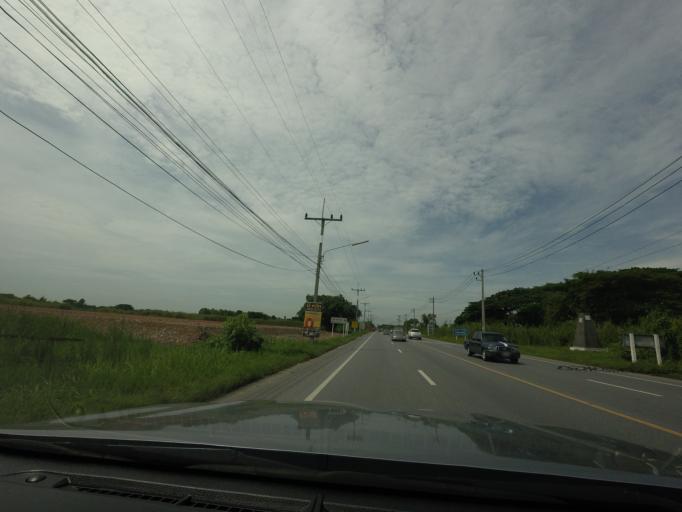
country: TH
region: Nakhon Si Thammarat
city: Nakhon Si Thammarat
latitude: 8.4421
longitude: 99.9827
